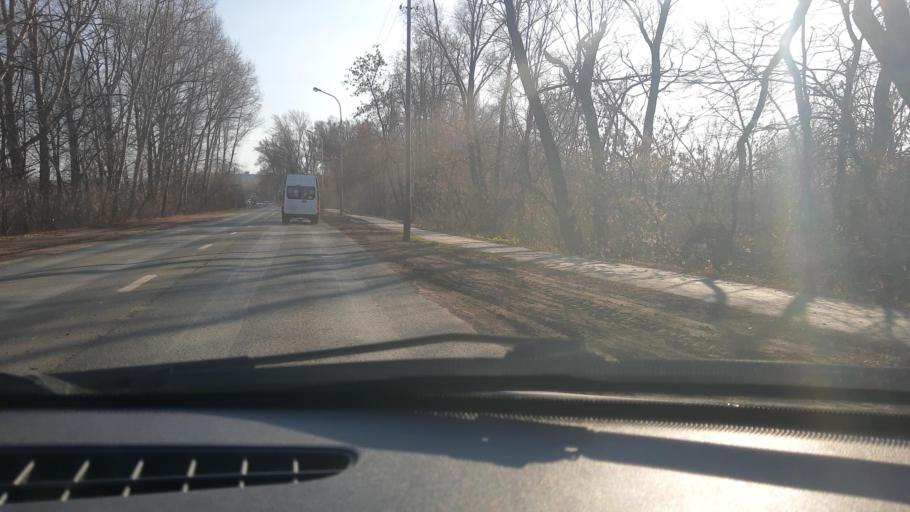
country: RU
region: Bashkortostan
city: Avdon
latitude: 54.7163
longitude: 55.8093
